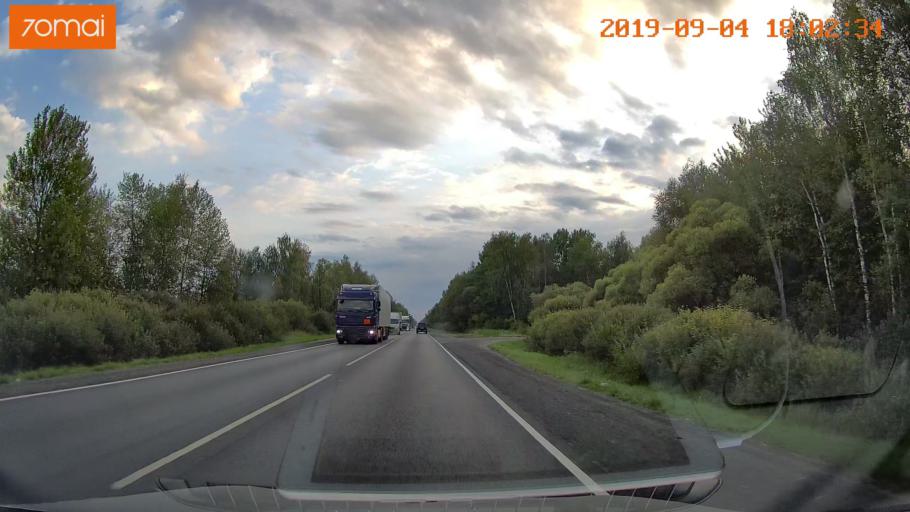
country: RU
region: Moskovskaya
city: Il'inskiy Pogost
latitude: 55.4728
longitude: 38.8632
